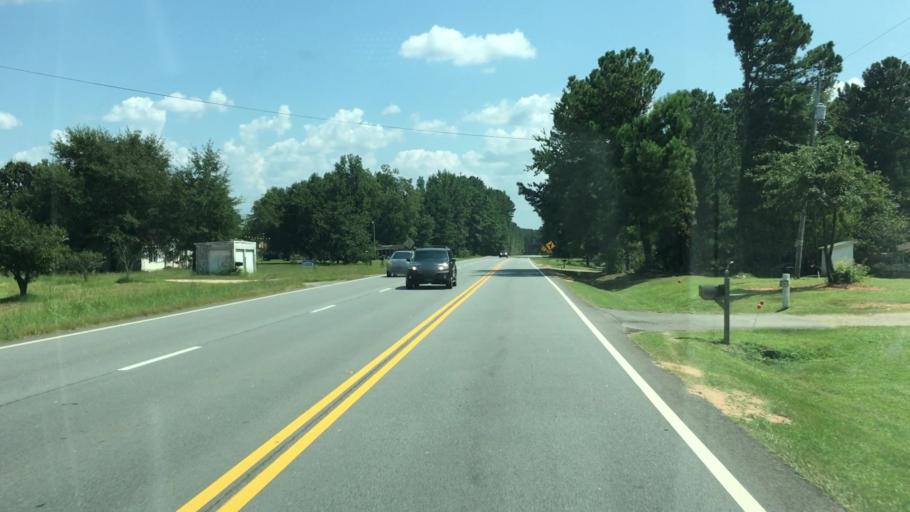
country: US
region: Georgia
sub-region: Oconee County
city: Watkinsville
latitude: 33.7420
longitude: -83.4308
